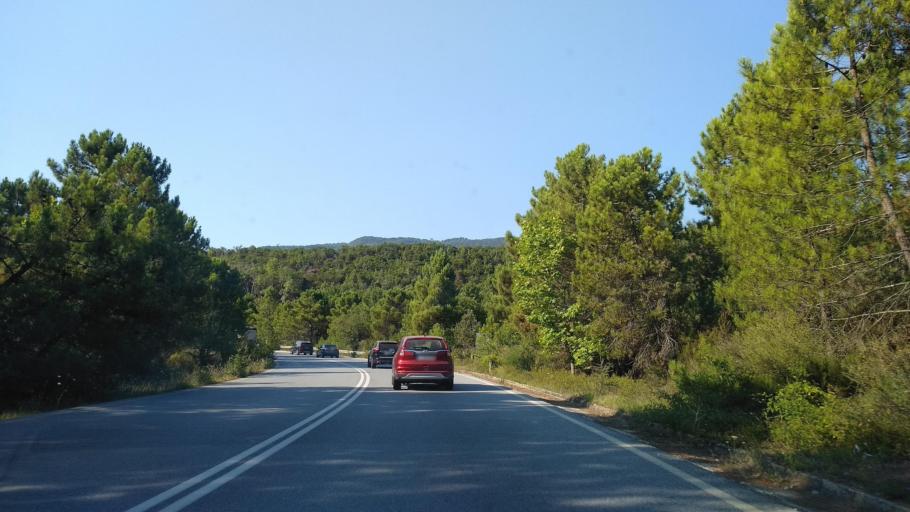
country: GR
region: Central Macedonia
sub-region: Nomos Chalkidikis
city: Stratonion
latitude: 40.5630
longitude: 23.8216
